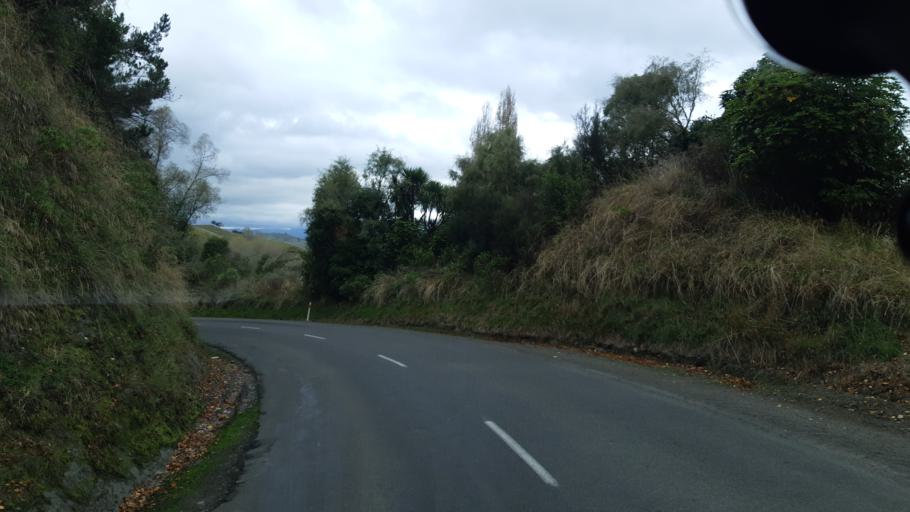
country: NZ
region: Manawatu-Wanganui
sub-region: Ruapehu District
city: Waiouru
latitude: -39.6507
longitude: 175.7369
